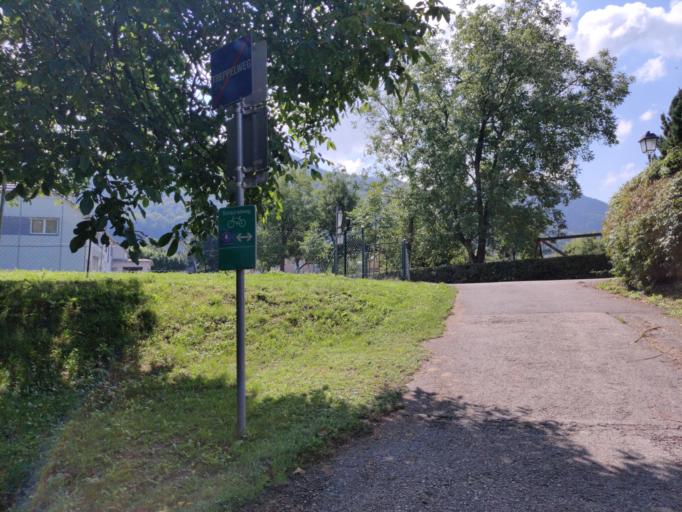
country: AT
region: Lower Austria
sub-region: Politischer Bezirk Krems
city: Spitz
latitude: 48.3648
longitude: 15.4289
